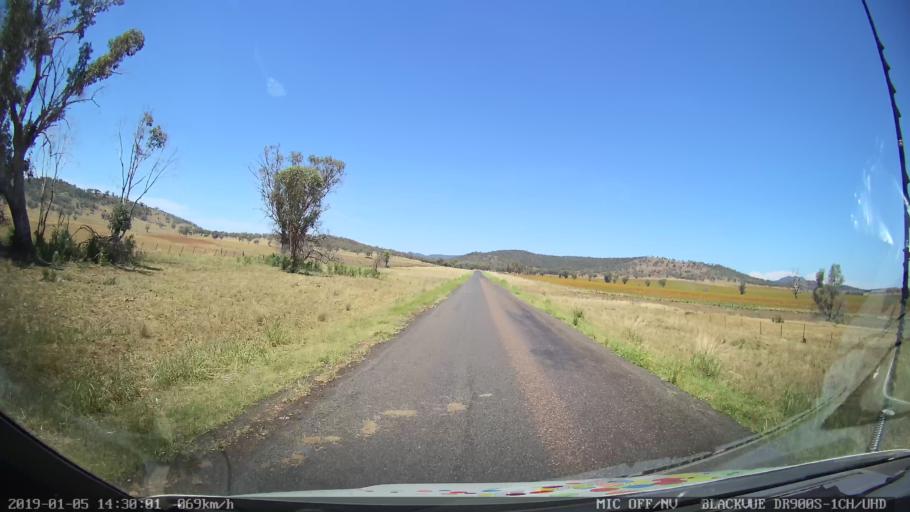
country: AU
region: New South Wales
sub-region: Tamworth Municipality
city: Phillip
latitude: -31.2281
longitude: 150.5872
